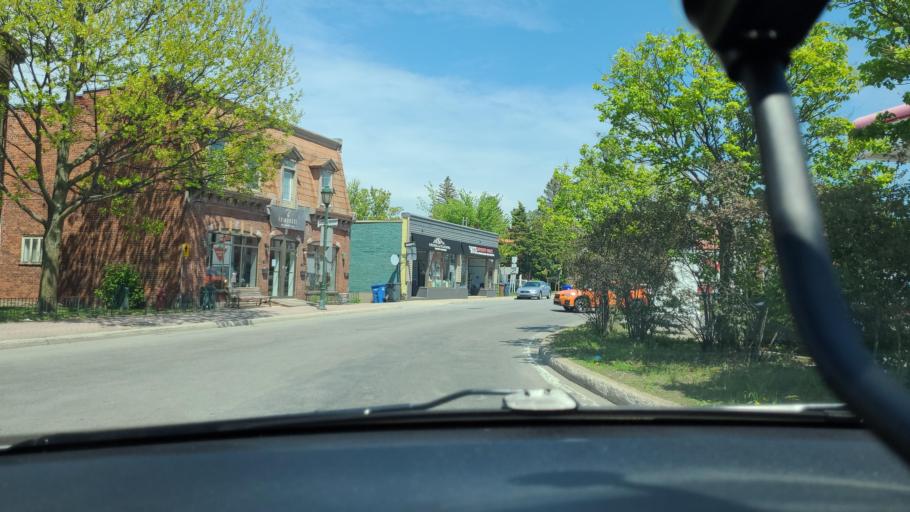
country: CA
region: Quebec
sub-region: Laurentides
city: Lachute
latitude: 45.6574
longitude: -74.3320
